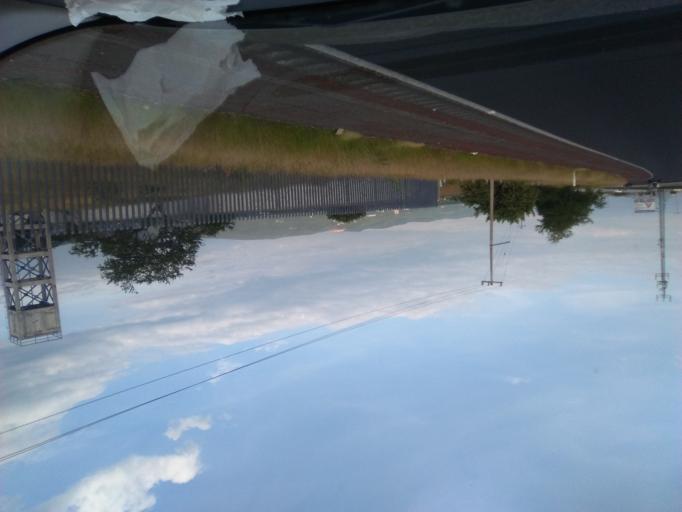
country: MX
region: Morelos
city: Alpuyeca
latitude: 18.7473
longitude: -99.2459
